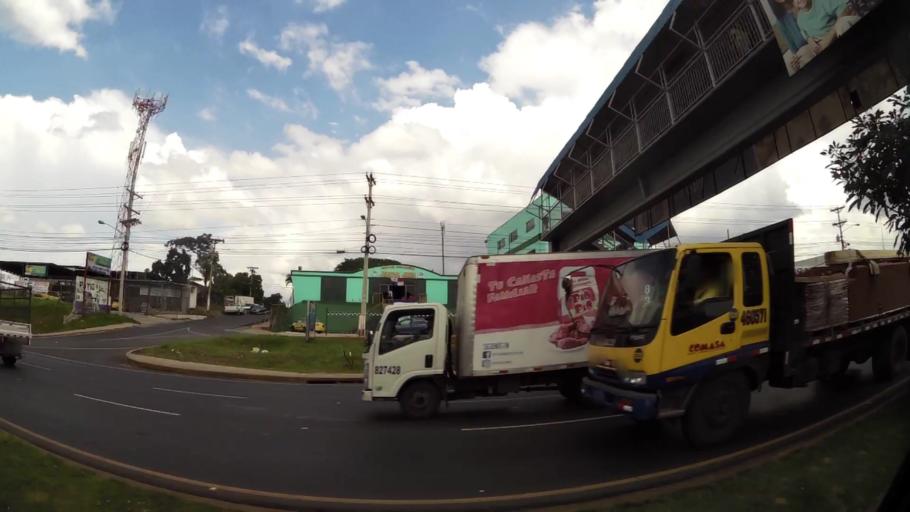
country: PA
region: Panama
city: Tocumen
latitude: 9.0621
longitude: -79.4224
